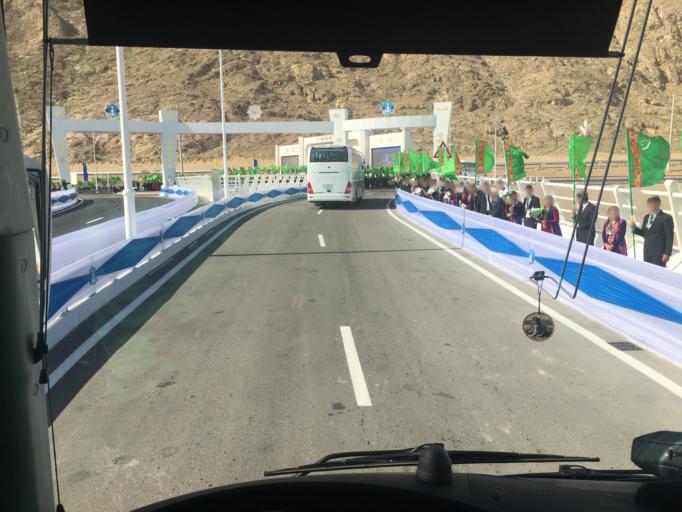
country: TM
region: Balkan
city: Turkmenbasy
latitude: 40.0071
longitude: 53.0240
